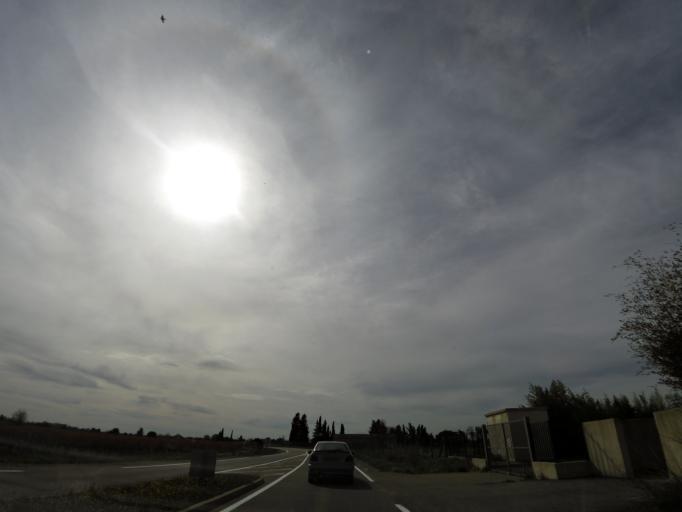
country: FR
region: Languedoc-Roussillon
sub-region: Departement du Gard
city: Gallargues-le-Montueux
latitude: 43.7147
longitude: 4.1824
